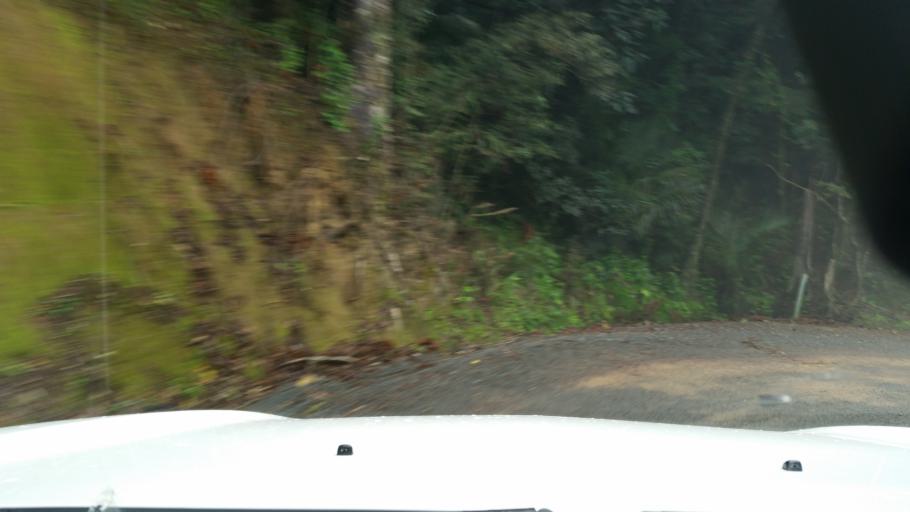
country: NZ
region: Northland
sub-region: Whangarei
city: Ruakaka
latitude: -35.7754
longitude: 174.5415
